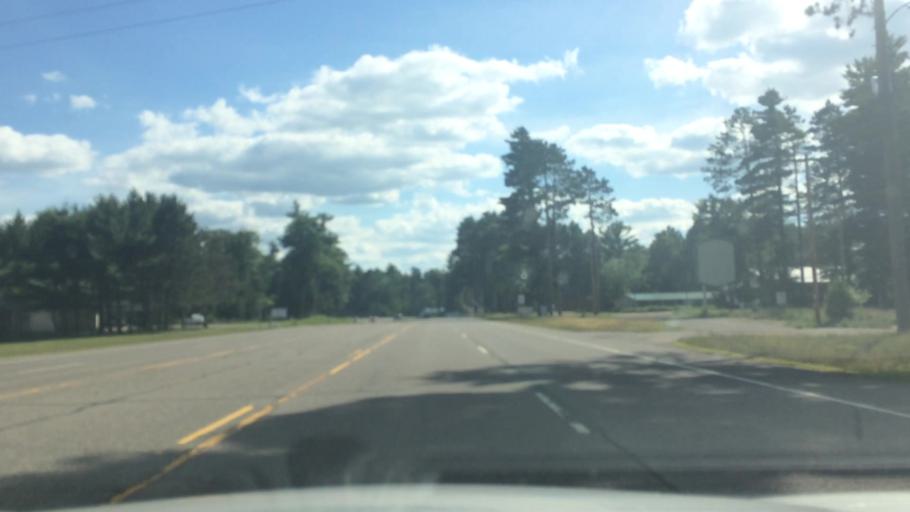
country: US
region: Wisconsin
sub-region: Vilas County
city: Lac du Flambeau
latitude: 45.8229
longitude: -89.7238
